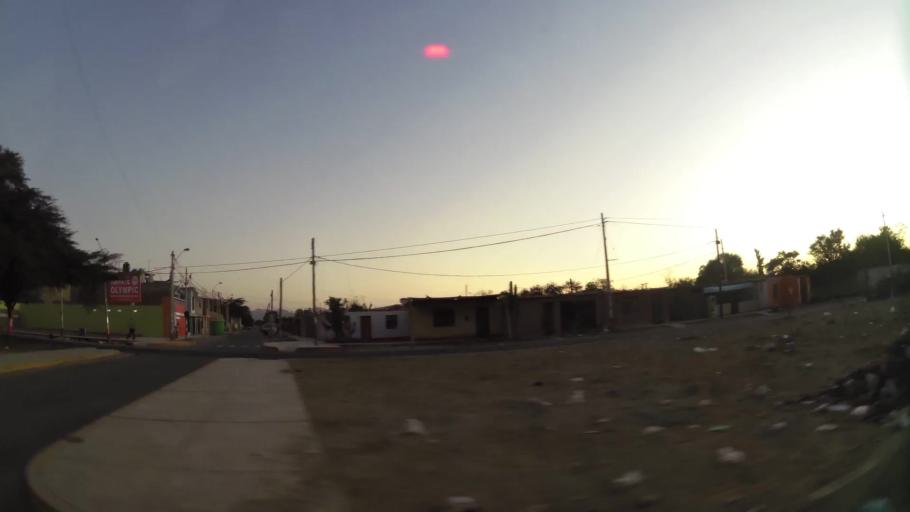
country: PE
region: Ica
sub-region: Provincia de Ica
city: Ica
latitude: -14.0829
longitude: -75.7289
